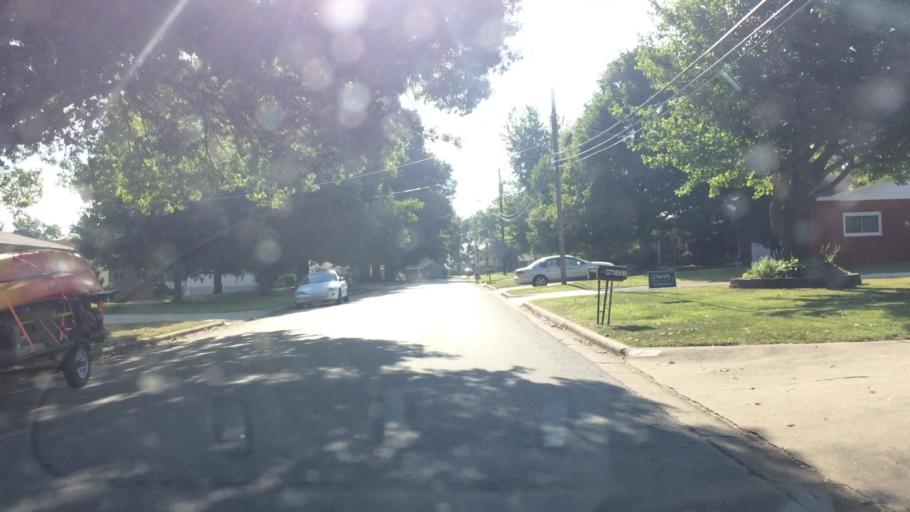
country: US
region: Missouri
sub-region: Greene County
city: Springfield
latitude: 37.2555
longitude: -93.2689
